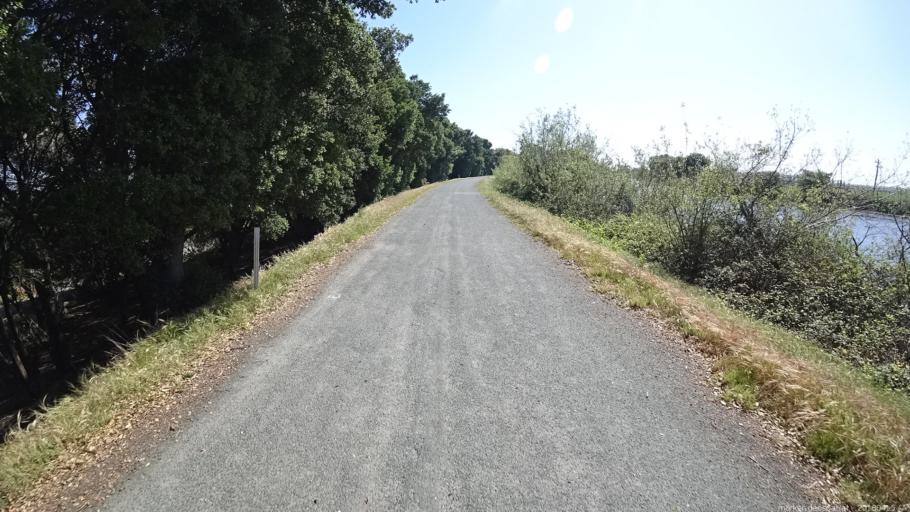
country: US
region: California
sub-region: Solano County
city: Rio Vista
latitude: 38.1246
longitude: -121.6730
